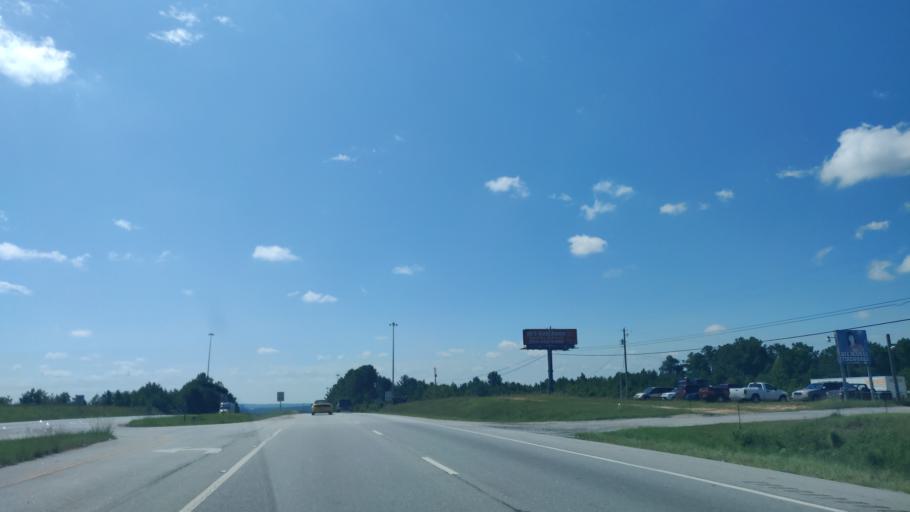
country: US
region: Alabama
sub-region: Russell County
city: Ladonia
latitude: 32.5115
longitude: -85.0591
